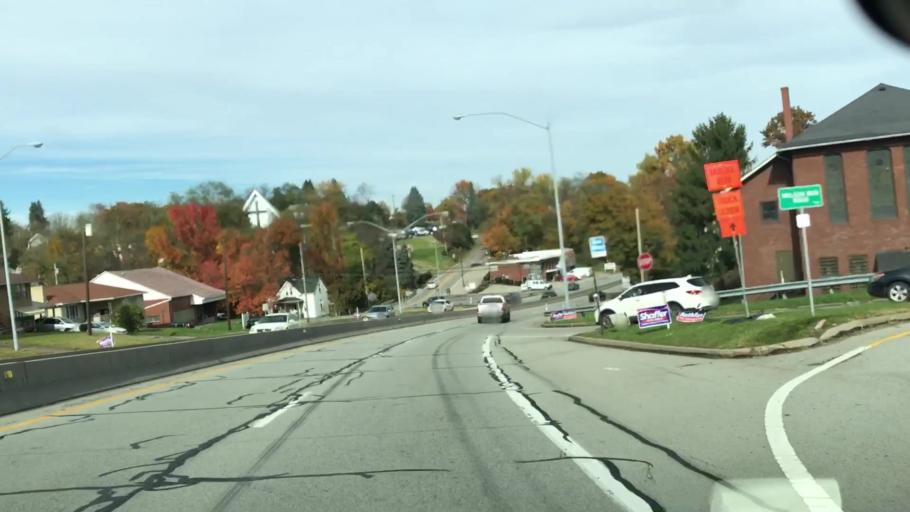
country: US
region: Pennsylvania
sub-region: Allegheny County
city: West View
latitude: 40.4990
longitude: -80.0129
